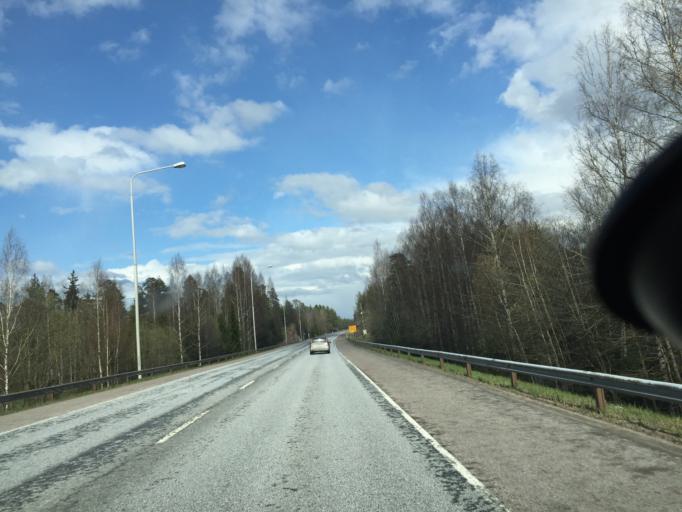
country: FI
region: Uusimaa
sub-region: Raaseporin
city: Karis
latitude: 60.0797
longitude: 23.7233
